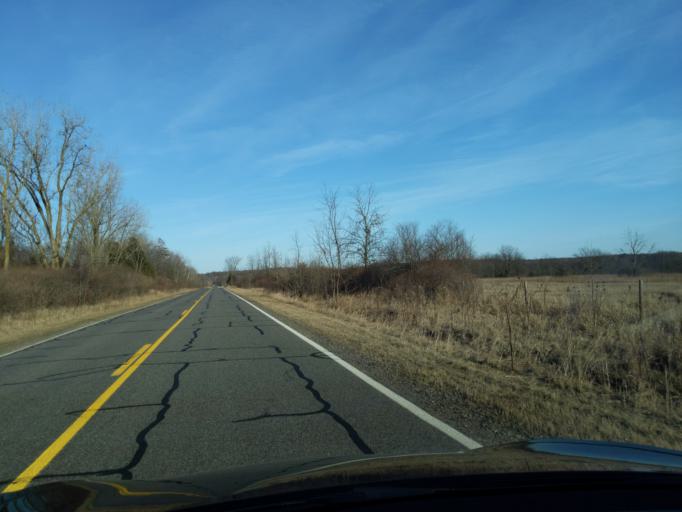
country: US
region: Michigan
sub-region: Ionia County
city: Ionia
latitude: 42.9554
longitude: -85.1402
